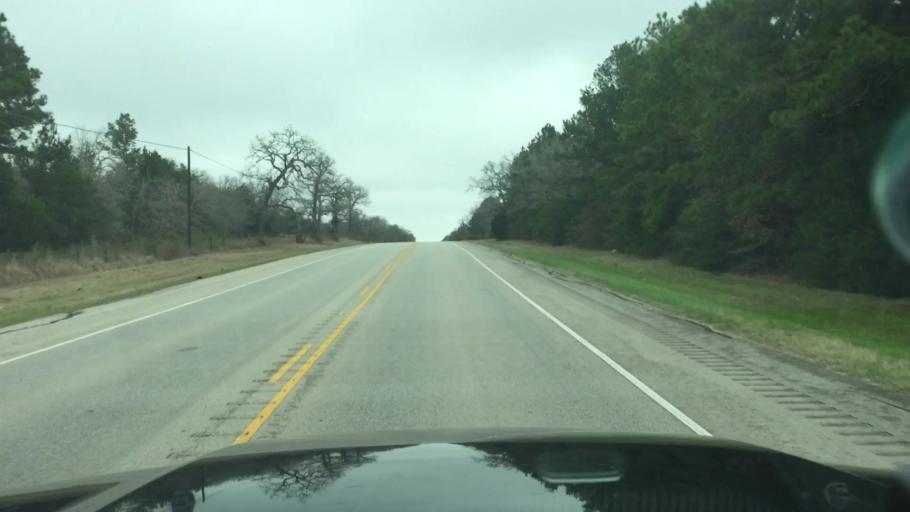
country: US
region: Texas
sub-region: Lee County
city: Giddings
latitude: 30.0718
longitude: -96.9168
